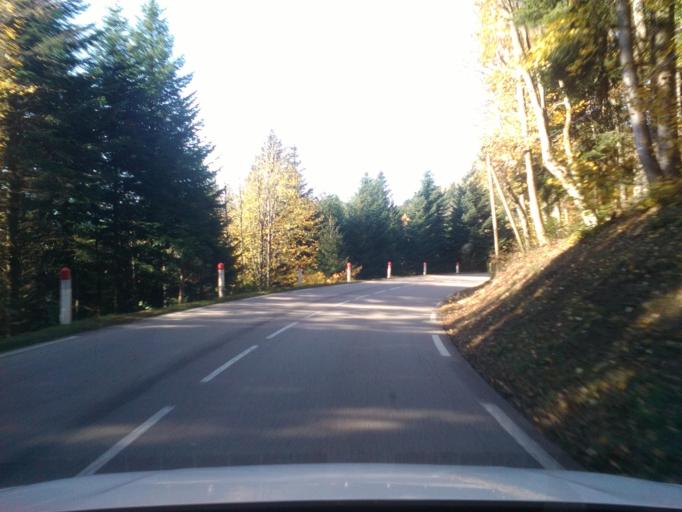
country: FR
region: Lorraine
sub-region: Departement des Vosges
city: Senones
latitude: 48.4082
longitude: 7.0758
